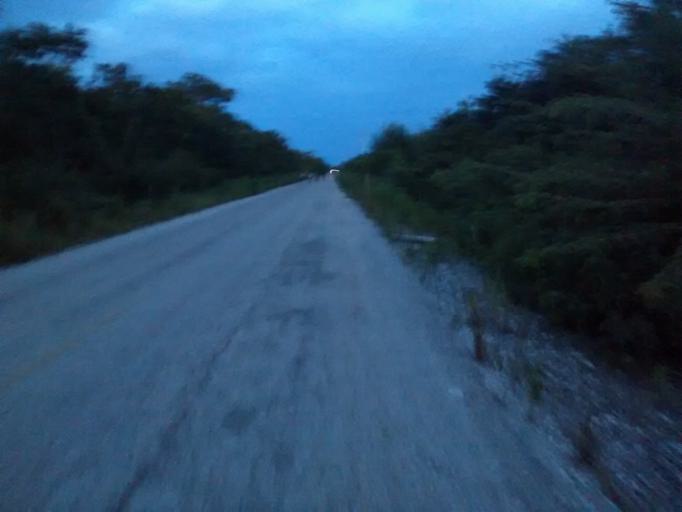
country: MX
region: Yucatan
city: Chichimila
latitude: 20.4638
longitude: -88.2250
